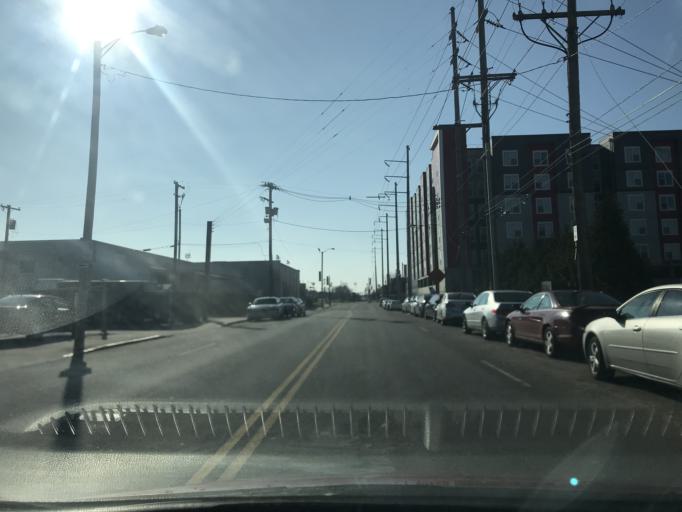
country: US
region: Kentucky
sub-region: Jefferson County
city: Audubon Park
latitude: 38.2205
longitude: -85.7541
